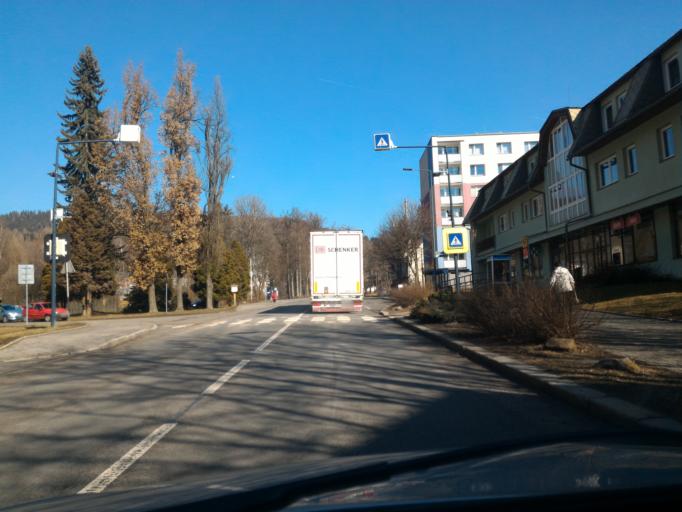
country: CZ
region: Liberecky
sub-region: Okres Jablonec nad Nisou
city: Desna
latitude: 50.7557
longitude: 15.3138
